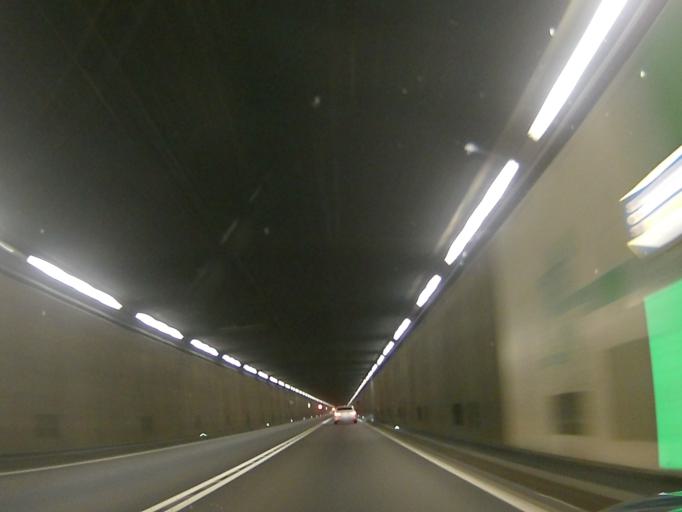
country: CH
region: Ticino
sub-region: Leventina District
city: Airolo
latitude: 46.5377
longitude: 8.5915
